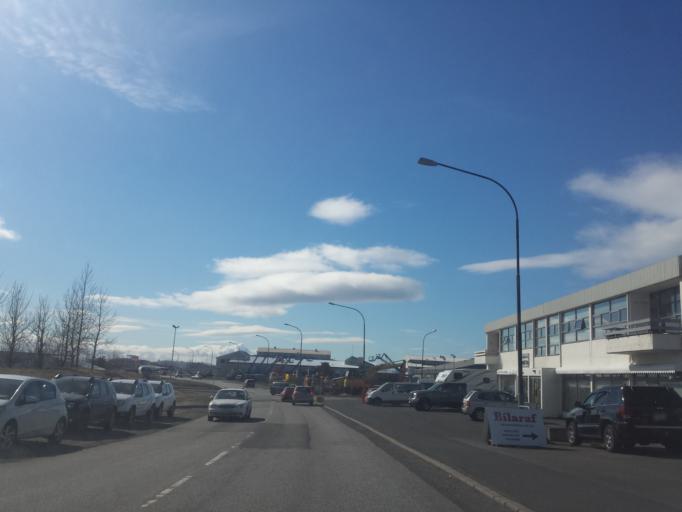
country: IS
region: Capital Region
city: Hafnarfjoerdur
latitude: 64.0774
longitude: -21.9340
